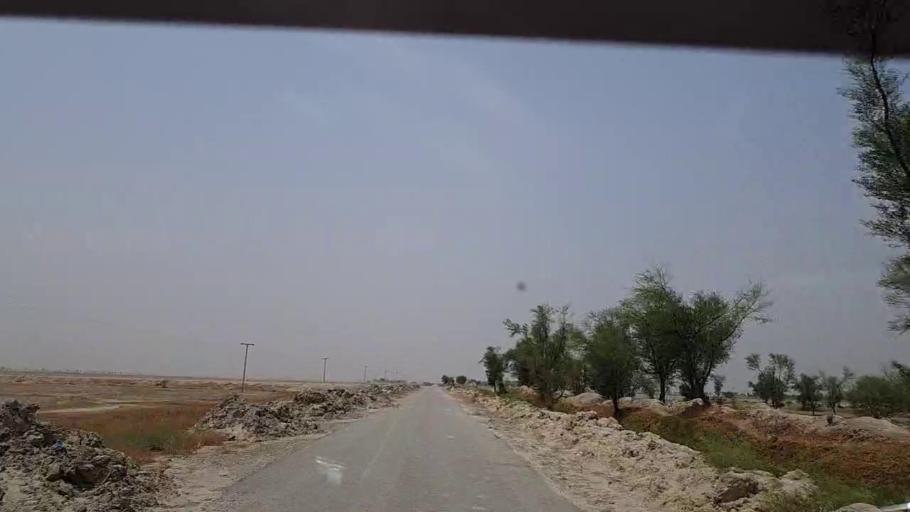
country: PK
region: Sindh
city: Khairpur Nathan Shah
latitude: 27.0320
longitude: 67.6197
